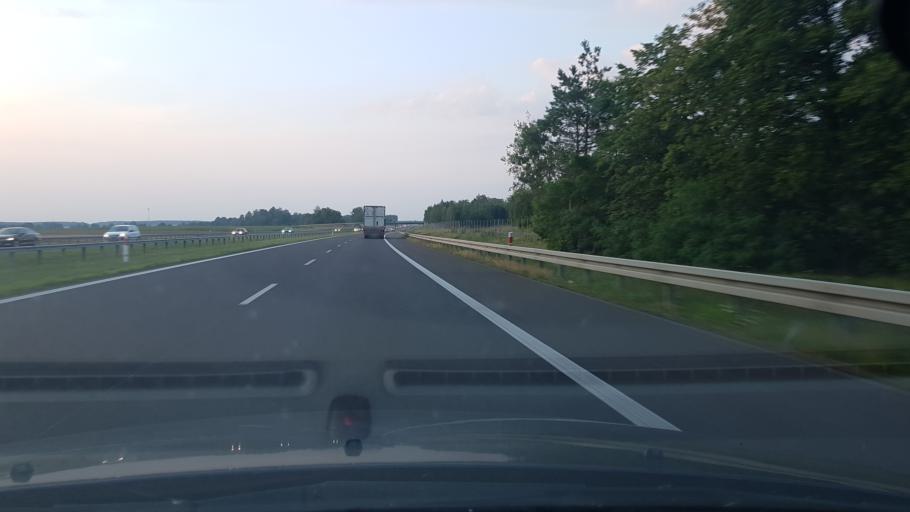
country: PL
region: Masovian Voivodeship
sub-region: Powiat mlawski
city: Wieczfnia Koscielna
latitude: 53.2579
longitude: 20.4257
